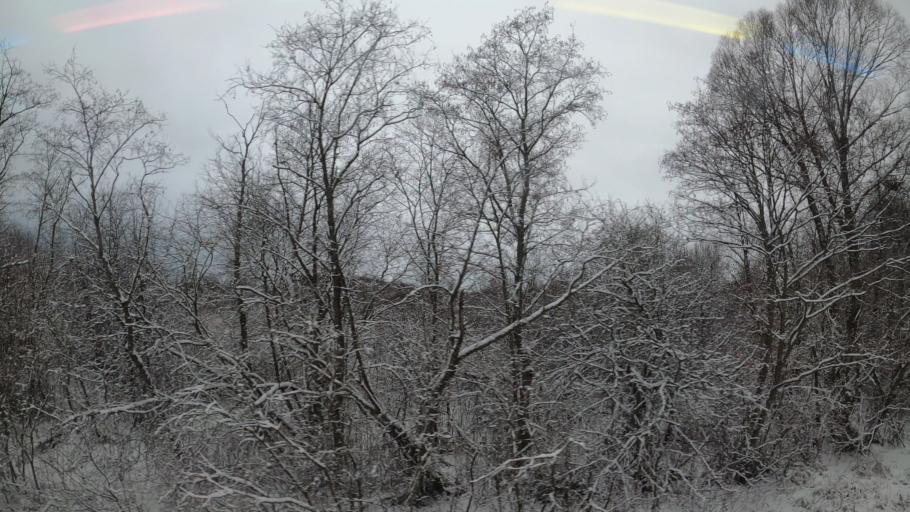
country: RU
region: Jaroslavl
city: Pereslavl'-Zalesskiy
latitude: 56.7191
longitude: 38.9079
